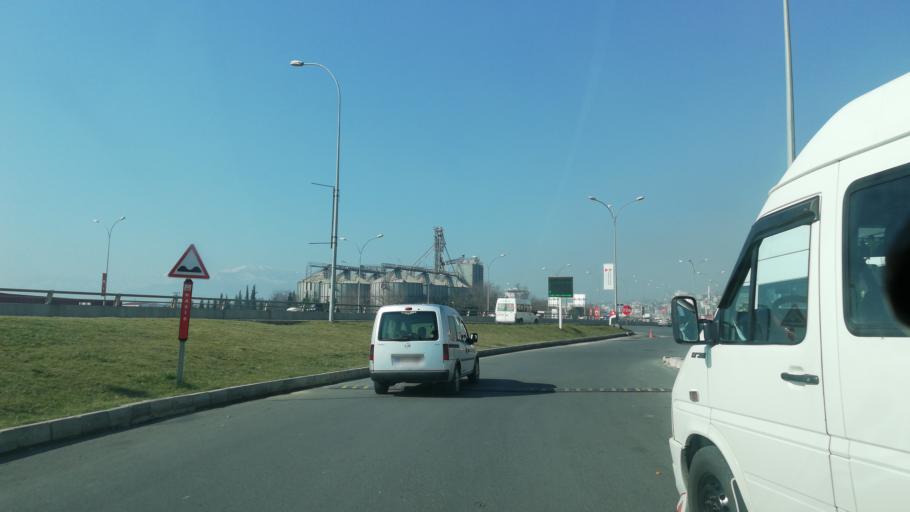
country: TR
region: Kahramanmaras
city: Kahramanmaras
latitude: 37.5691
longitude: 36.9238
